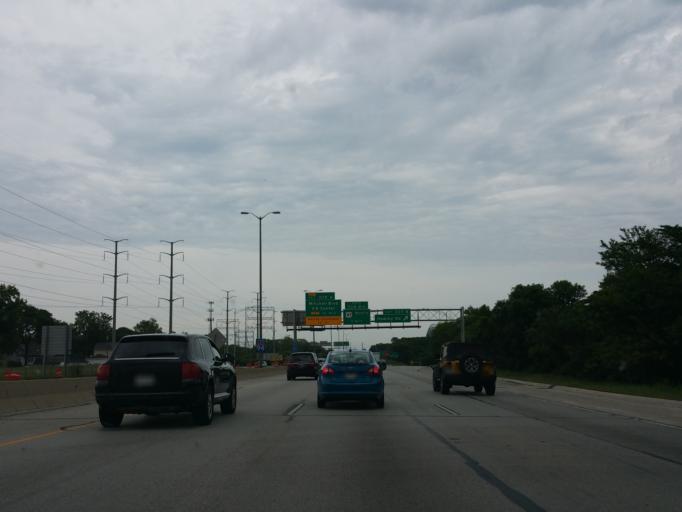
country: US
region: Wisconsin
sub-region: Milwaukee County
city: West Allis
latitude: 43.0304
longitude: -87.9917
